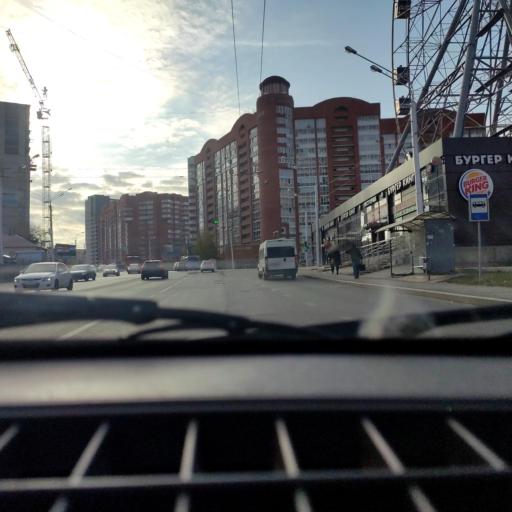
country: RU
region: Bashkortostan
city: Ufa
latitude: 54.7142
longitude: 55.9959
